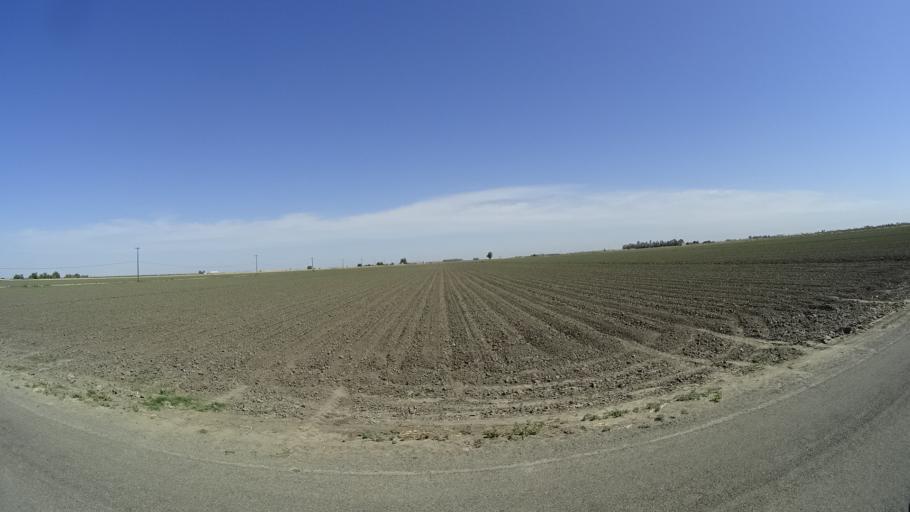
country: US
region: California
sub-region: Kings County
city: Stratford
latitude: 36.1967
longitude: -119.8151
